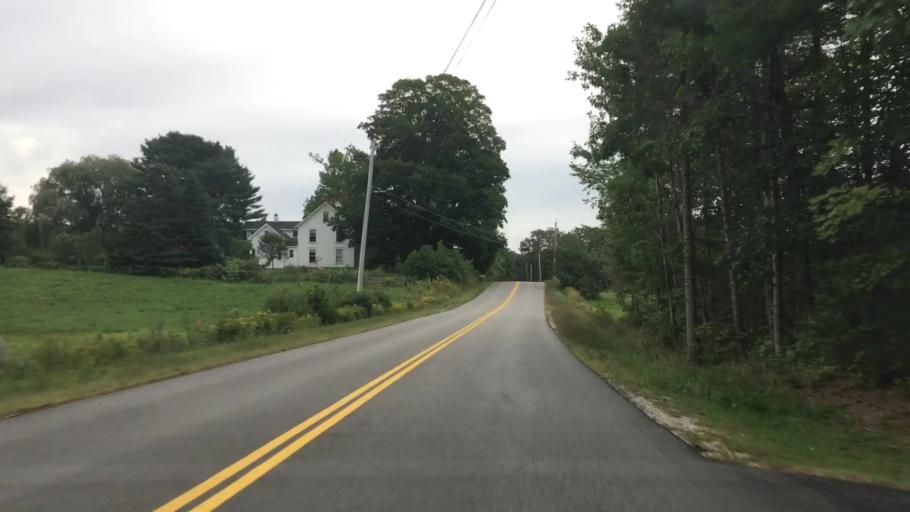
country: US
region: Maine
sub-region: Cumberland County
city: New Gloucester
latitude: 43.9178
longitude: -70.2453
